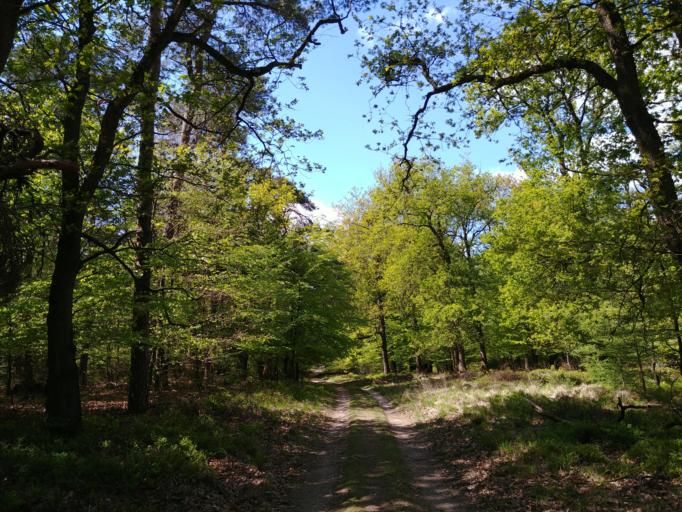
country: NL
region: Gelderland
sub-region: Gemeente Apeldoorn
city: Uddel
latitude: 52.2416
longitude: 5.8667
